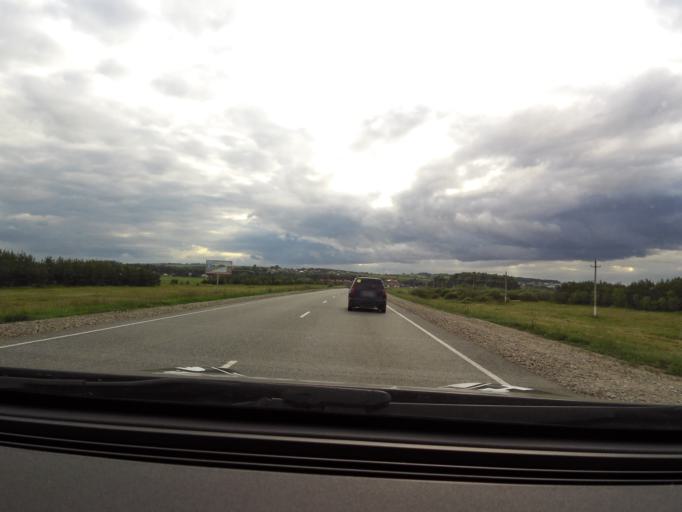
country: RU
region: Tatarstan
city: Sviyazhsk
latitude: 55.7091
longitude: 48.6719
